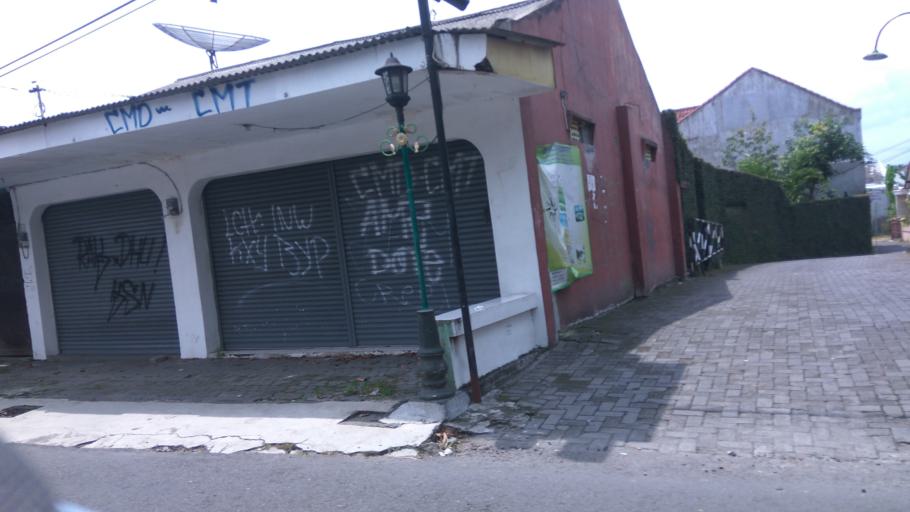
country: ID
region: Daerah Istimewa Yogyakarta
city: Depok
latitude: -7.7455
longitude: 110.4142
